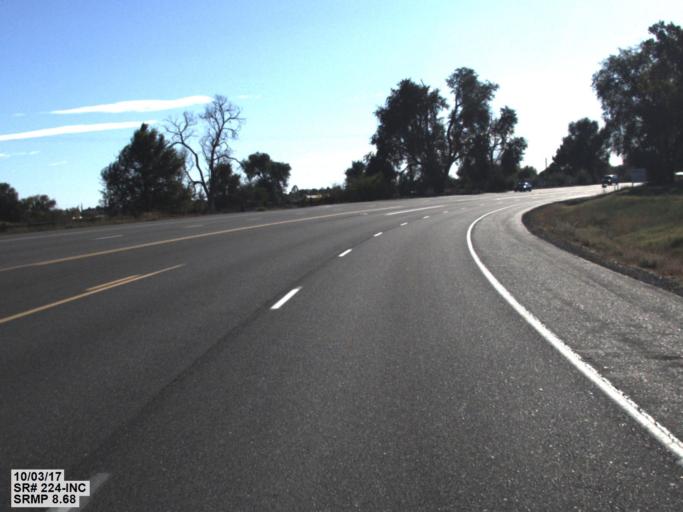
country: US
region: Washington
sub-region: Benton County
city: West Richland
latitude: 46.2981
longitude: -119.3278
